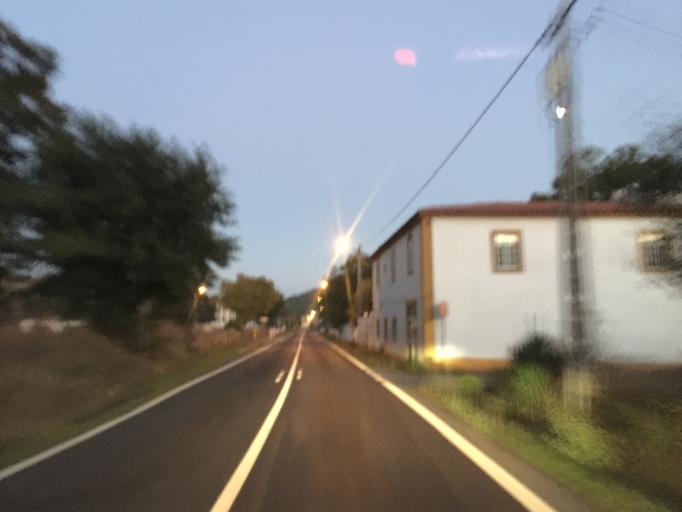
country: PT
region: Portalegre
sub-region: Marvao
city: Marvao
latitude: 39.3881
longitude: -7.4056
